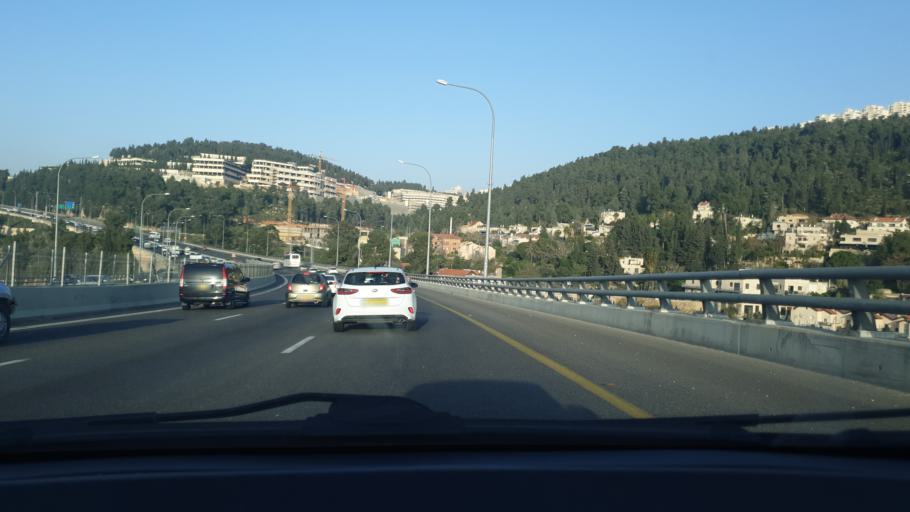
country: PS
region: West Bank
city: Bayt Iksa
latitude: 31.7942
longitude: 35.1653
